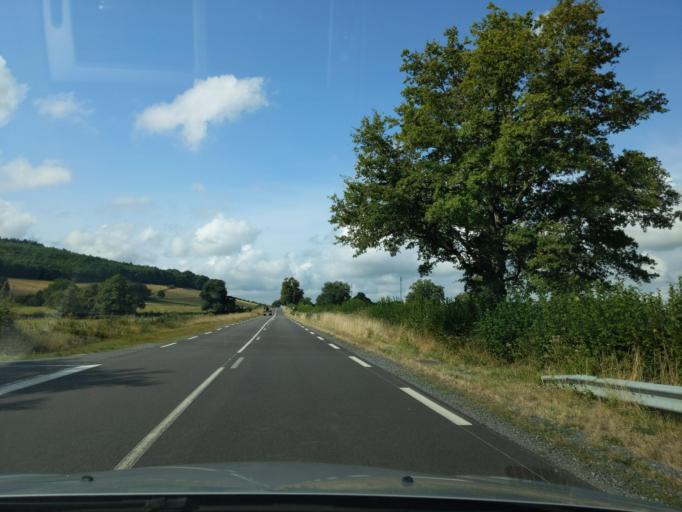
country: FR
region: Bourgogne
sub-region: Departement de la Nievre
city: Luzy
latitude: 46.8415
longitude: 4.0535
